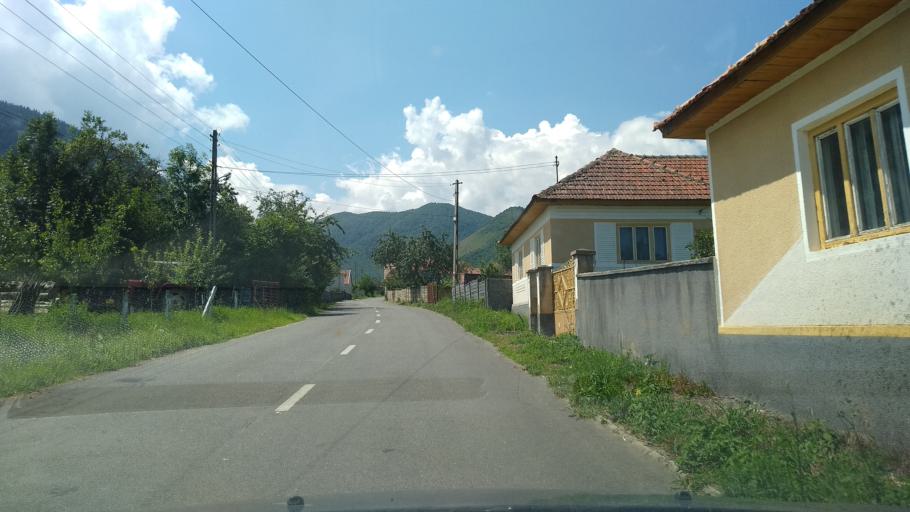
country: RO
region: Hunedoara
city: Salasu de Sus
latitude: 45.4808
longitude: 22.9164
